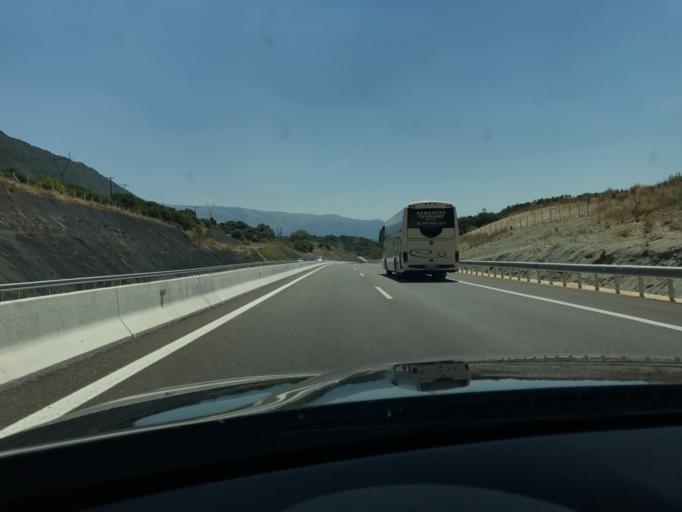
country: GR
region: Epirus
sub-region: Nomos Ioanninon
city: Agia Kyriaki
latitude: 39.4891
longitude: 20.8908
